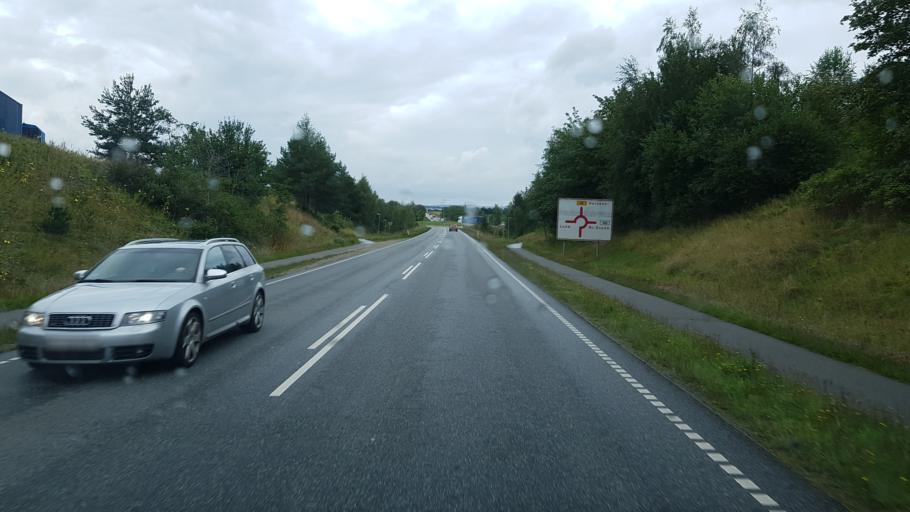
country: DK
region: Central Jutland
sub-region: Horsens Kommune
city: Horsens
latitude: 55.8993
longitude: 9.7497
